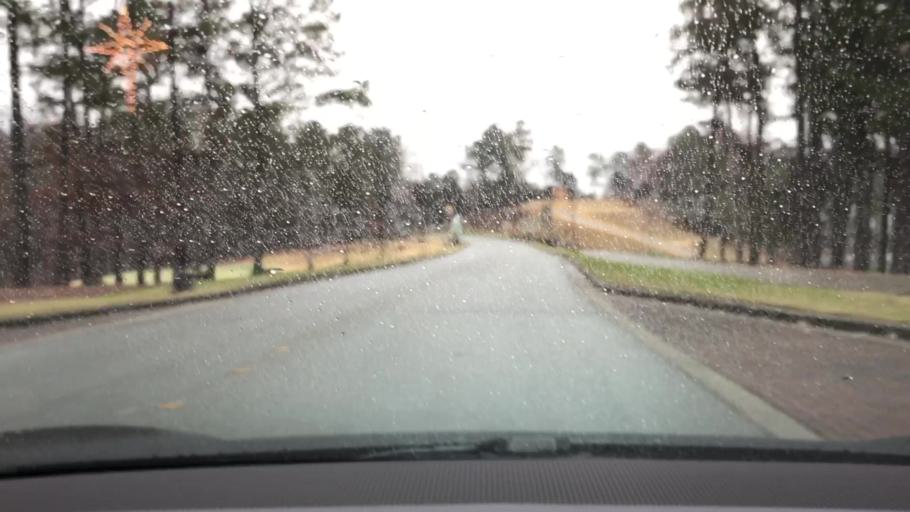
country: US
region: Georgia
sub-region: Gwinnett County
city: Buford
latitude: 34.1796
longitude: -84.0208
